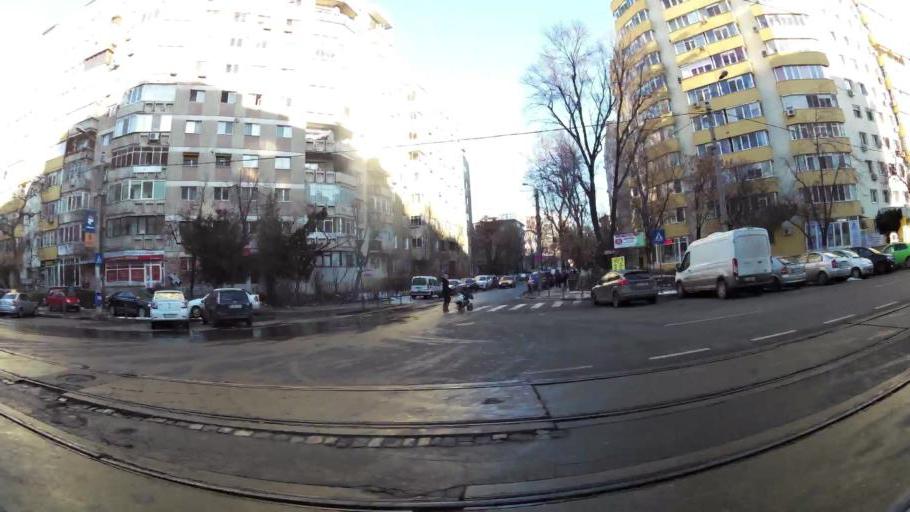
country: RO
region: Ilfov
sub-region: Comuna Fundeni-Dobroesti
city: Fundeni
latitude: 44.4366
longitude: 26.1595
